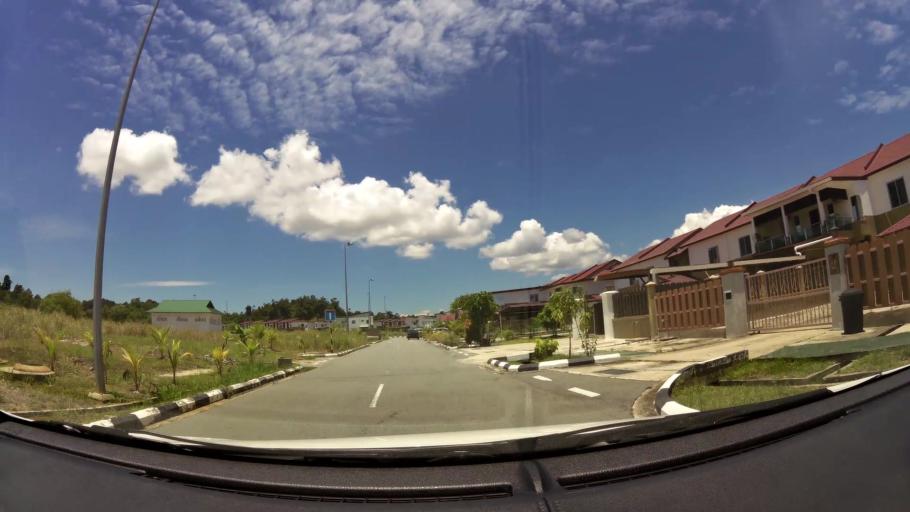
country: BN
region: Brunei and Muara
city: Bandar Seri Begawan
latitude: 5.0076
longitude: 115.0086
